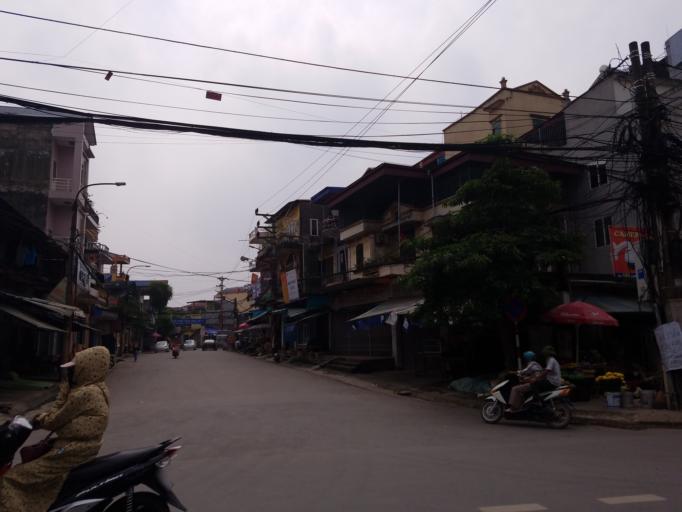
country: VN
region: Thai Nguyen
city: Thanh Pho Thai Nguyen
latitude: 21.5856
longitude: 105.8324
